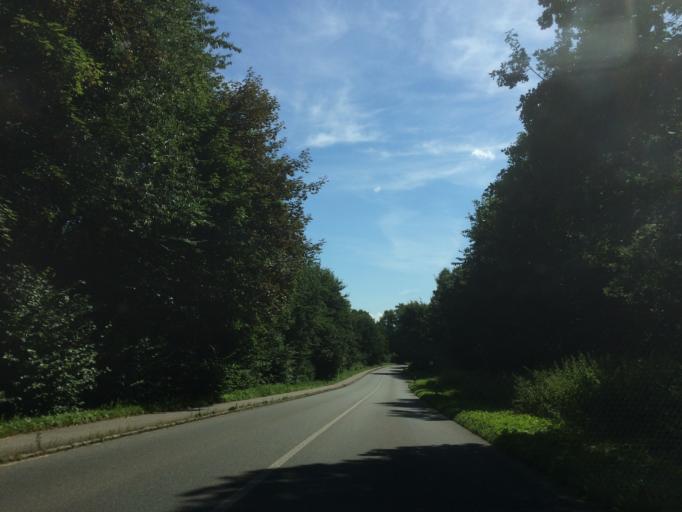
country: DE
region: Schleswig-Holstein
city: Eutin
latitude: 54.1545
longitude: 10.6037
